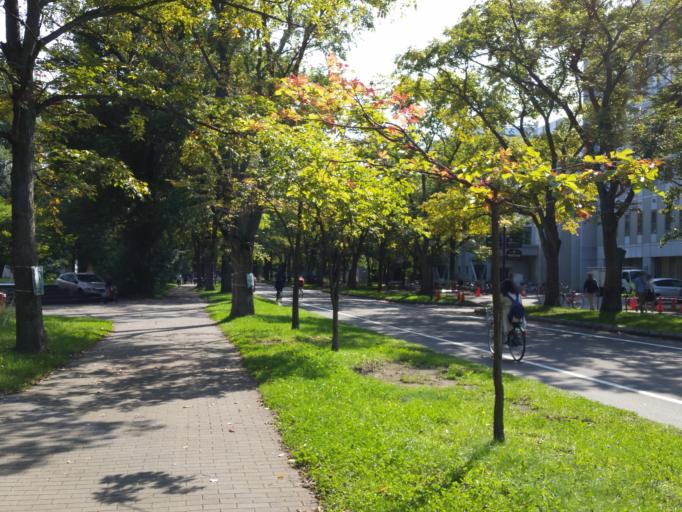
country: JP
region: Hokkaido
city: Sapporo
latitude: 43.0793
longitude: 141.3410
